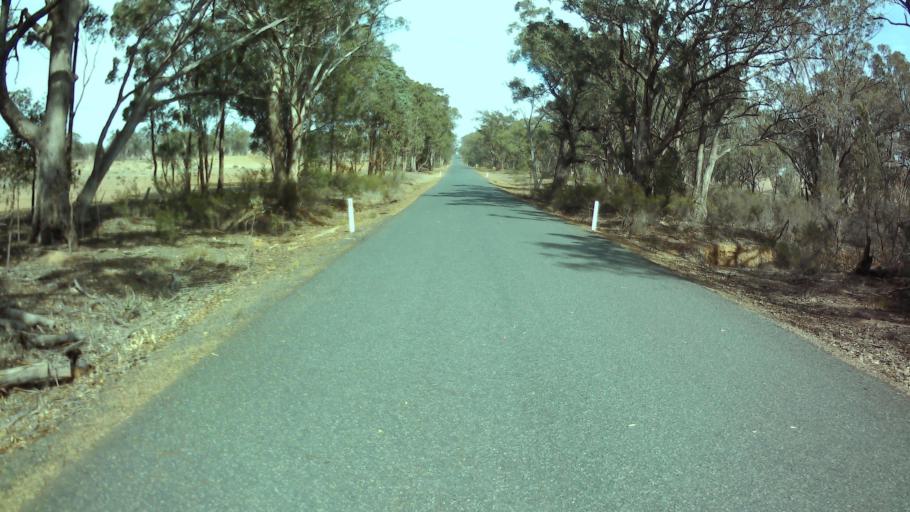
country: AU
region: New South Wales
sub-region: Weddin
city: Grenfell
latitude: -33.8075
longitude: 148.0565
